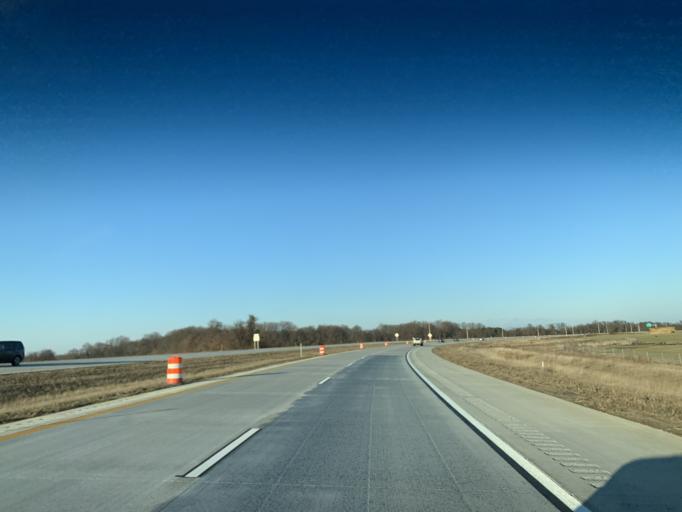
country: US
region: Delaware
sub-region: New Castle County
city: Middletown
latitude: 39.5190
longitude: -75.6908
